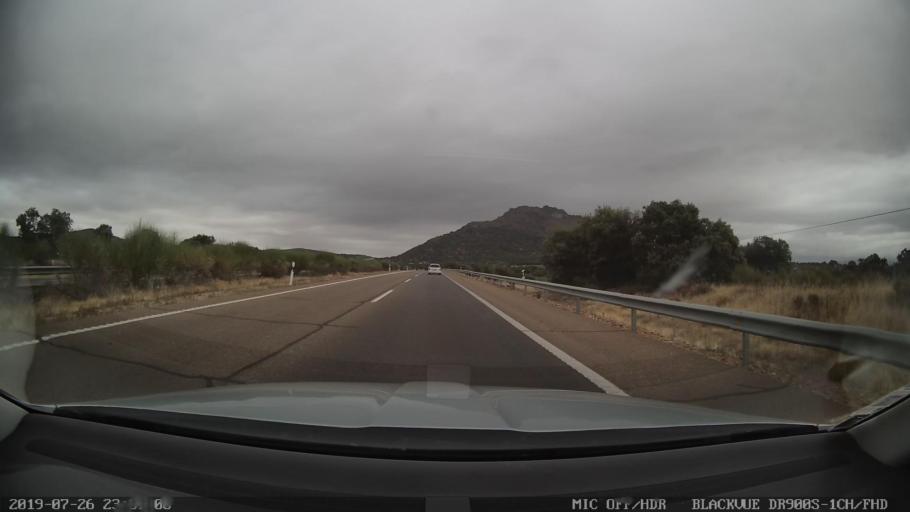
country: ES
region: Extremadura
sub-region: Provincia de Caceres
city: Puerto de Santa Cruz
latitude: 39.2923
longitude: -5.8553
